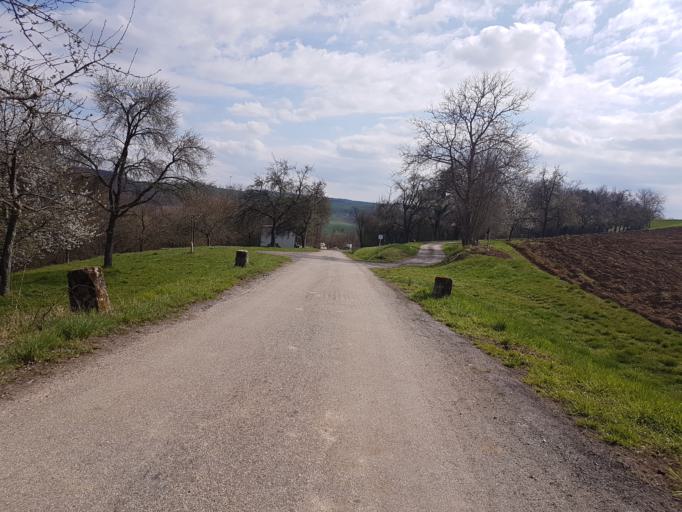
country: DE
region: Baden-Wuerttemberg
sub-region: Regierungsbezirk Stuttgart
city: Weissbach
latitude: 49.3591
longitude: 9.5664
